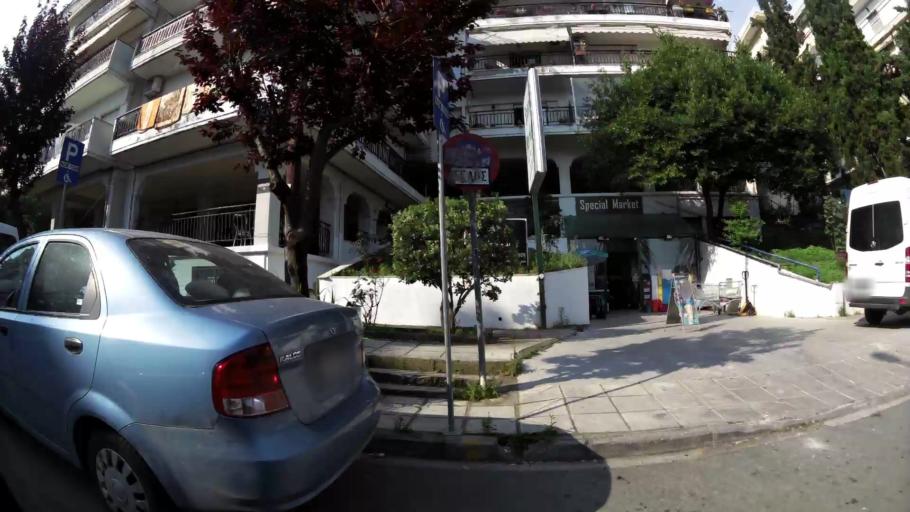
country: GR
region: Central Macedonia
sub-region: Nomos Thessalonikis
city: Sykies
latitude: 40.6539
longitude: 22.9558
